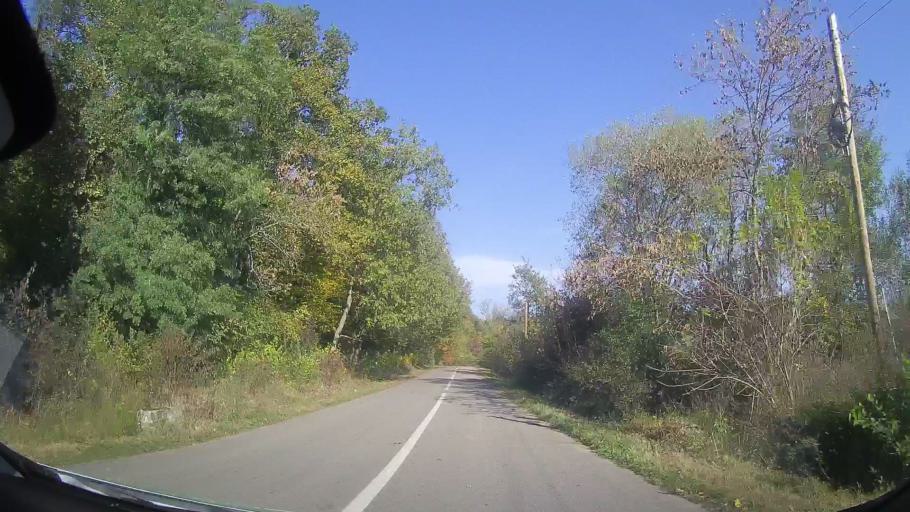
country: RO
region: Timis
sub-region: Comuna Ghizela
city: Ghizela
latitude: 45.8394
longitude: 21.7785
